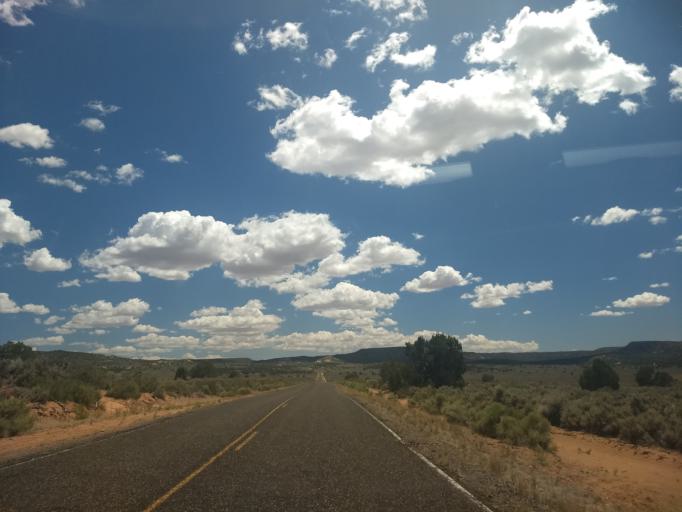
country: US
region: Utah
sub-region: Kane County
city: Kanab
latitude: 37.1684
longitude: -112.6633
